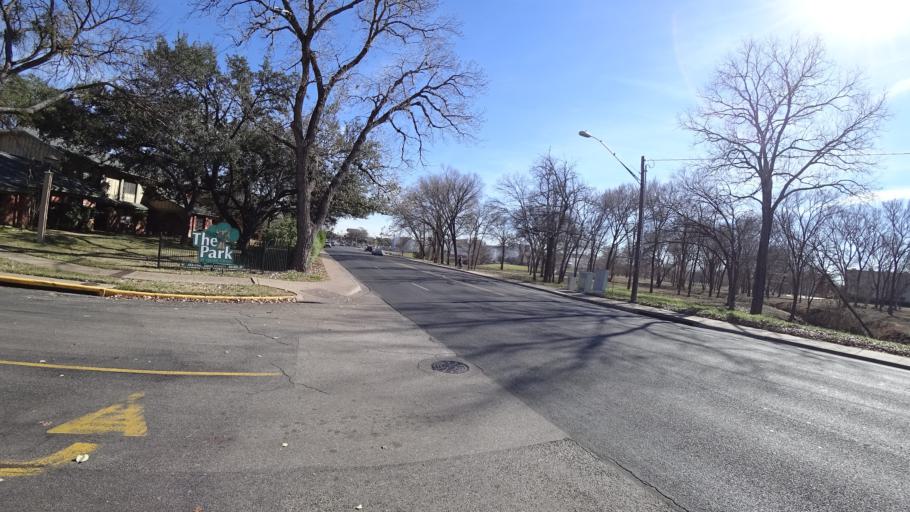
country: US
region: Texas
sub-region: Travis County
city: Wells Branch
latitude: 30.3664
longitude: -97.6993
